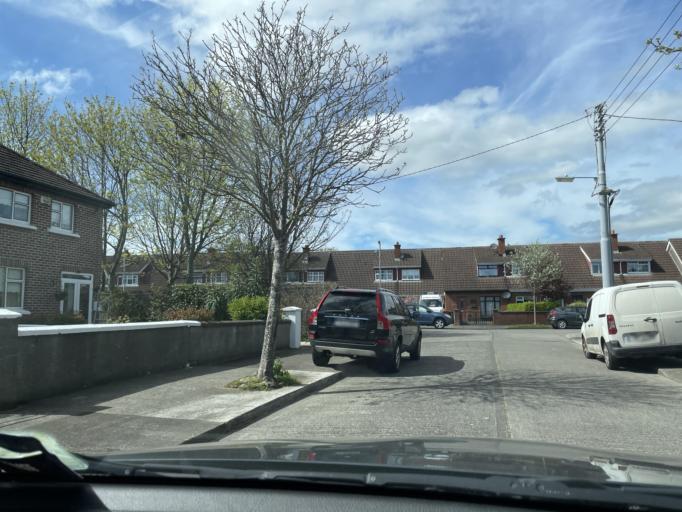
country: IE
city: Donnycarney
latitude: 53.3779
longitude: -6.2077
